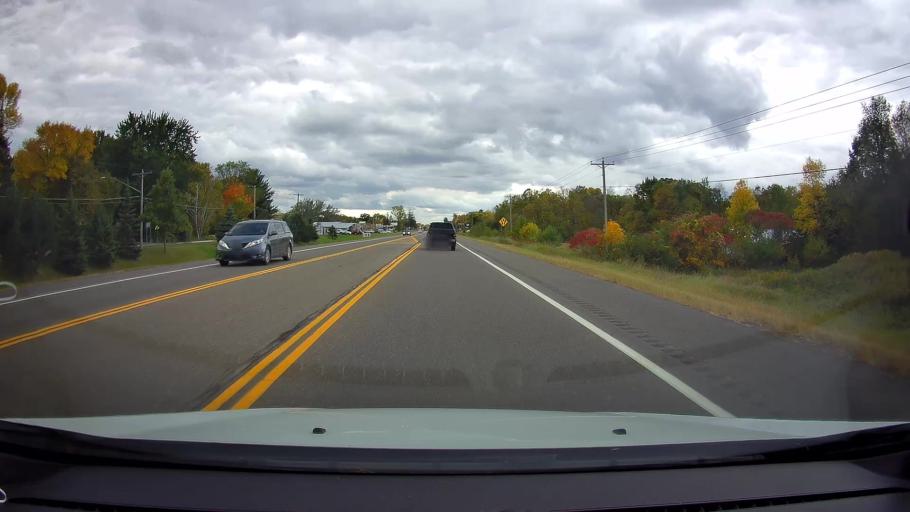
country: US
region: Minnesota
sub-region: Chisago County
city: Chisago City
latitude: 45.3782
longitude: -92.8765
